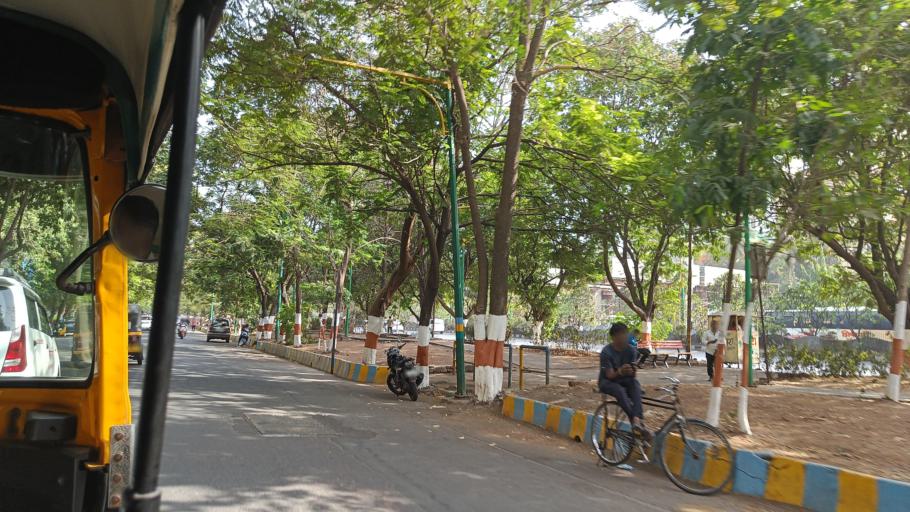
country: IN
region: Maharashtra
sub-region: Thane
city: Thane
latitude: 19.1947
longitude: 72.9630
